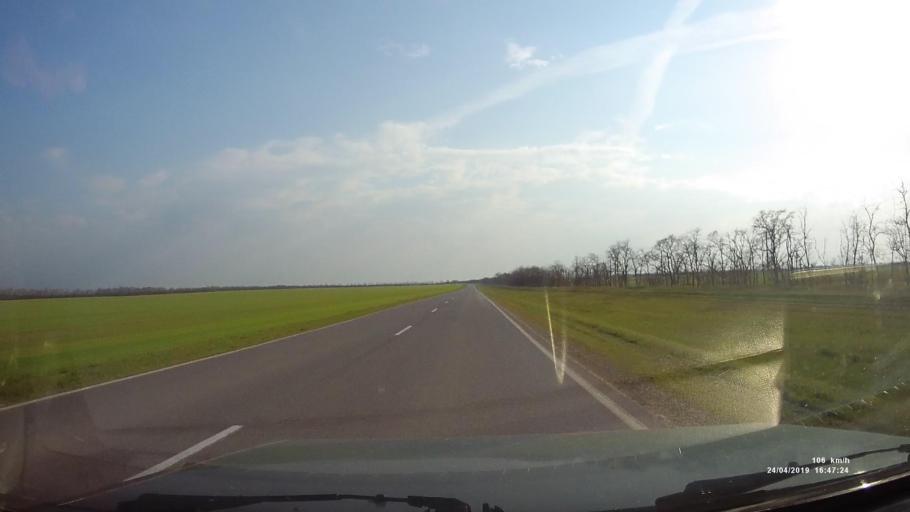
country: RU
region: Rostov
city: Proletarsk
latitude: 46.7443
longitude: 41.7878
